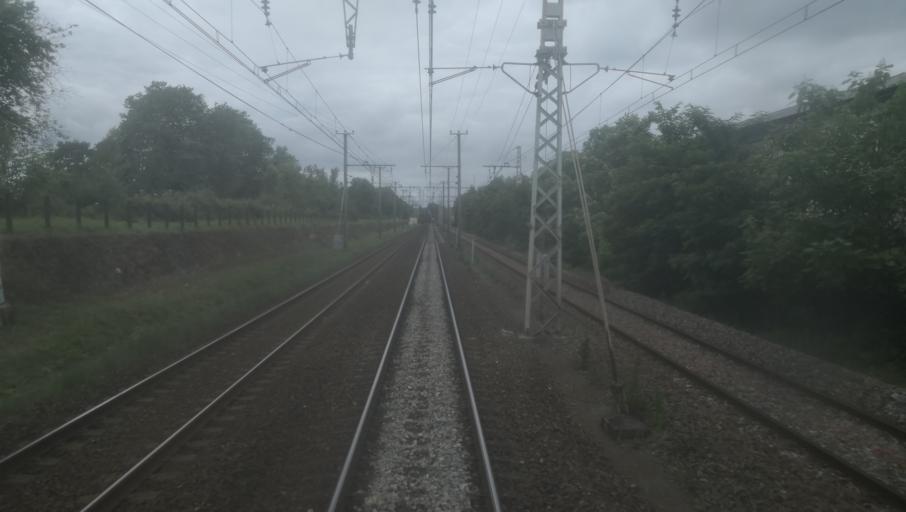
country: FR
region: Midi-Pyrenees
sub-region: Departement de la Haute-Garonne
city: Aucamville
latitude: 43.6610
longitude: 1.4164
